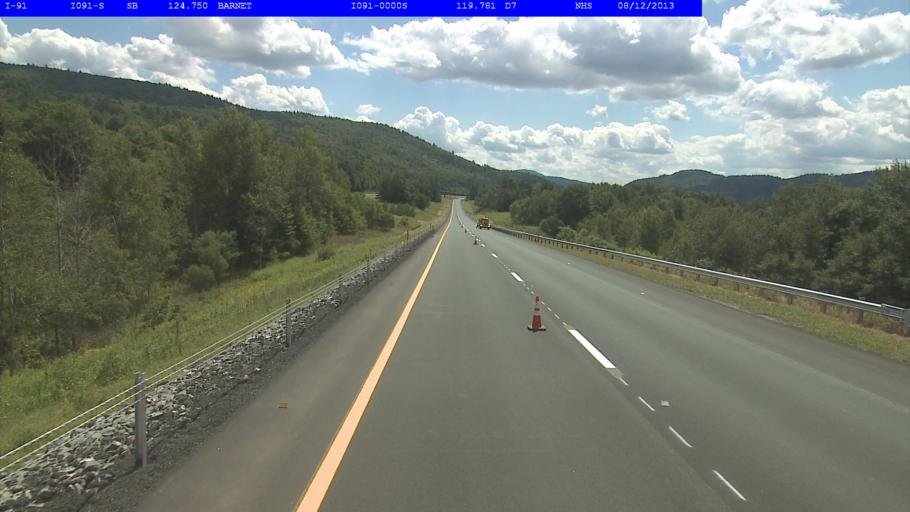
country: US
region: Vermont
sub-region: Caledonia County
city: Saint Johnsbury
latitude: 44.3488
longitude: -72.0353
